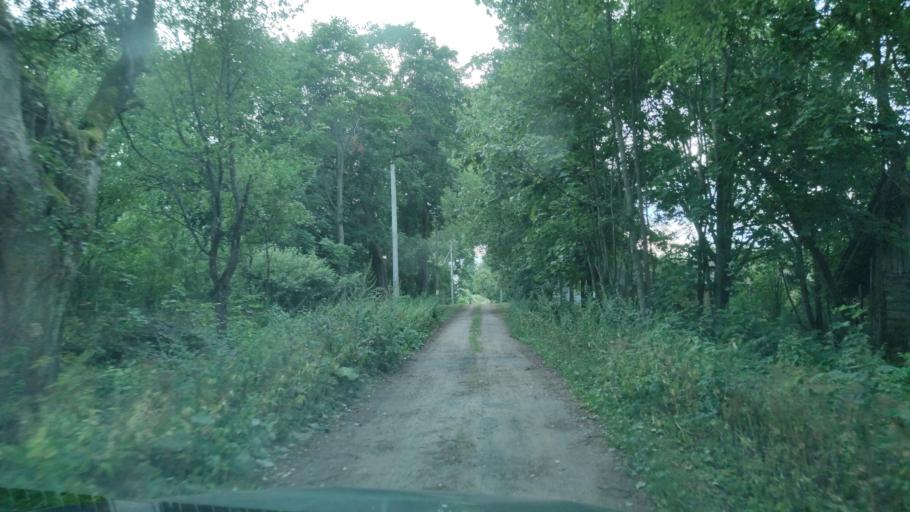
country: BY
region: Vitebsk
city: Mosar
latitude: 55.1241
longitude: 27.1740
